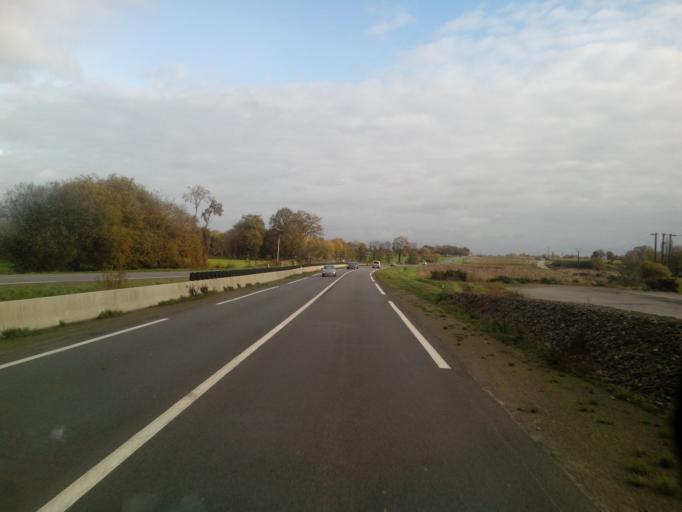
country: FR
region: Brittany
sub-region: Departement d'Ille-et-Vilaine
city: Saint-Meen-le-Grand
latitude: 48.1905
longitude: -2.1368
